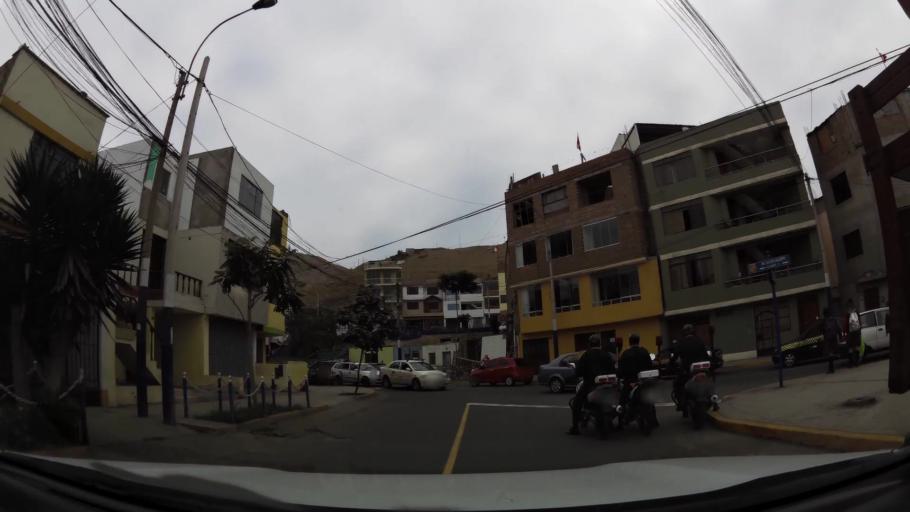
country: PE
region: Lima
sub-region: Lima
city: Surco
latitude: -12.1733
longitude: -77.0254
